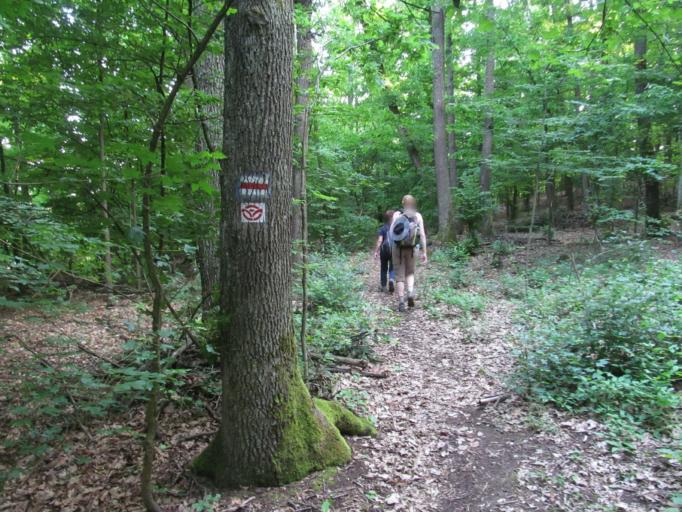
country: HU
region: Borsod-Abauj-Zemplen
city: Gonc
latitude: 48.5263
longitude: 21.4432
